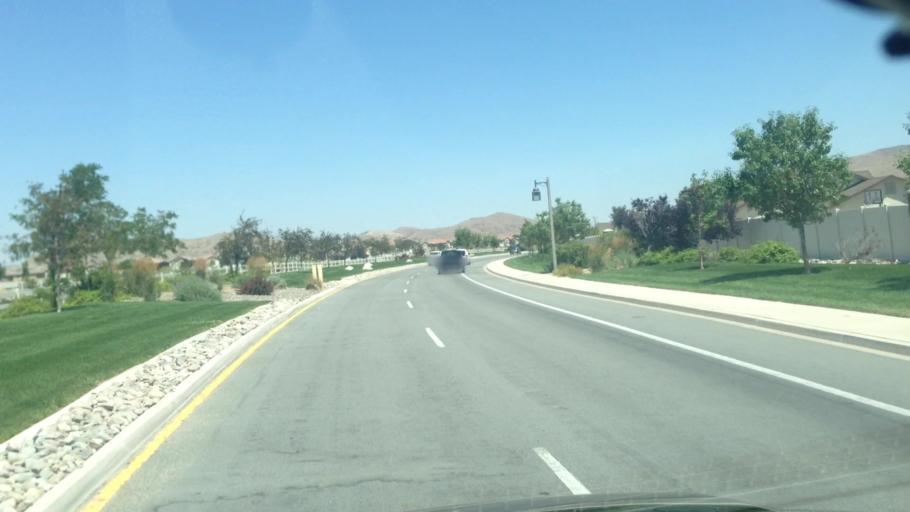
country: US
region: Nevada
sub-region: Washoe County
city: Sparks
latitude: 39.4368
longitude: -119.7299
